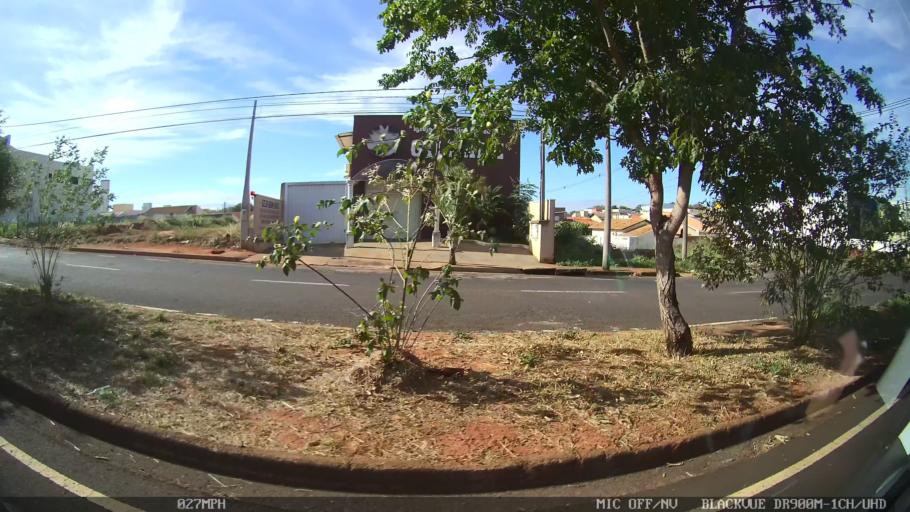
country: BR
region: Sao Paulo
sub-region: Sao Jose Do Rio Preto
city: Sao Jose do Rio Preto
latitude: -20.7905
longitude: -49.3497
